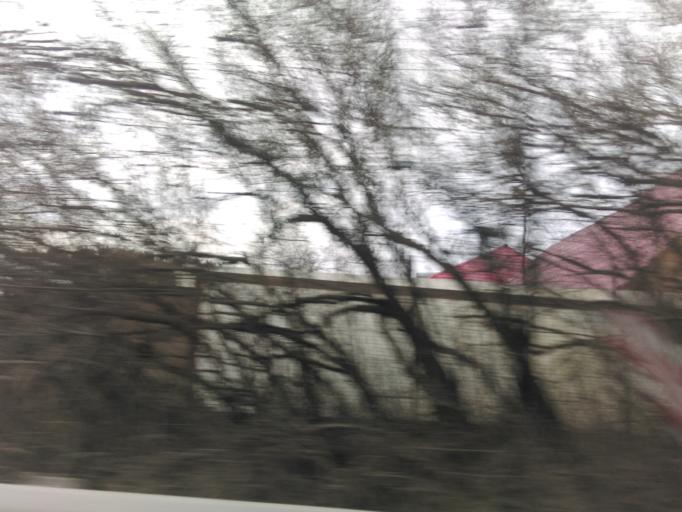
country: RU
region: Moskovskaya
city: Barvikha
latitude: 55.7466
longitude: 37.3060
